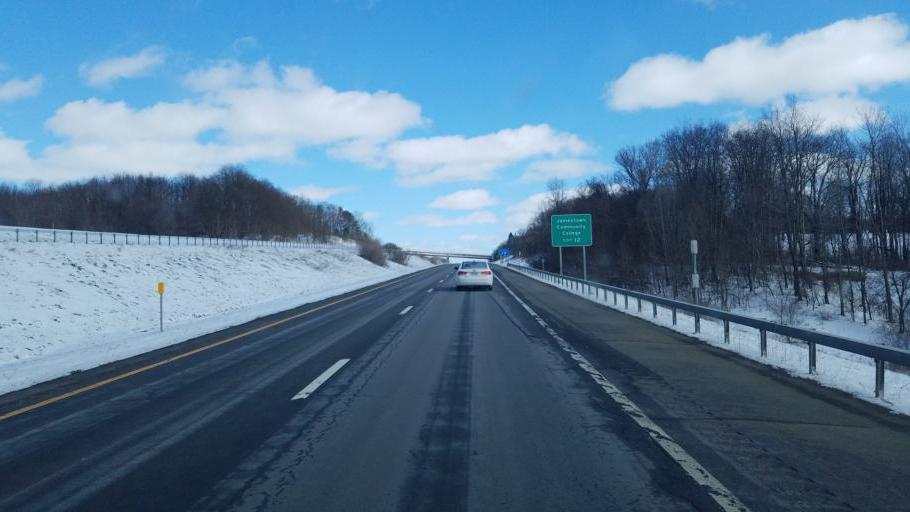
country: US
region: New York
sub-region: Chautauqua County
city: Jamestown
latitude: 42.1201
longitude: -79.2530
